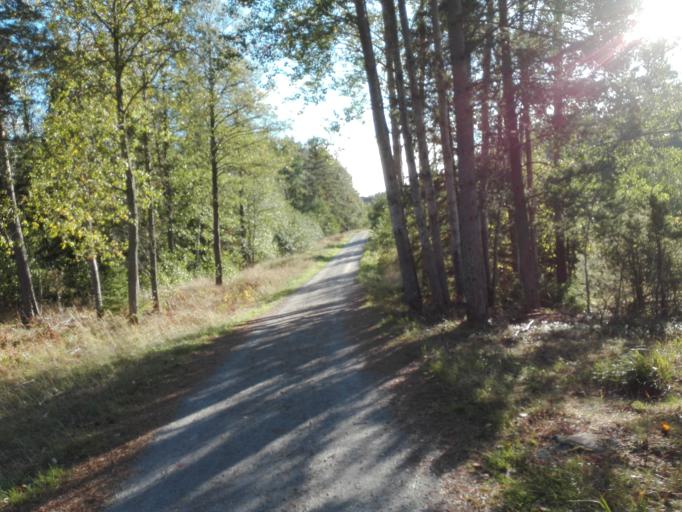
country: SE
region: Stockholm
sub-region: Nacka Kommun
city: Fisksatra
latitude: 59.2856
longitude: 18.2355
